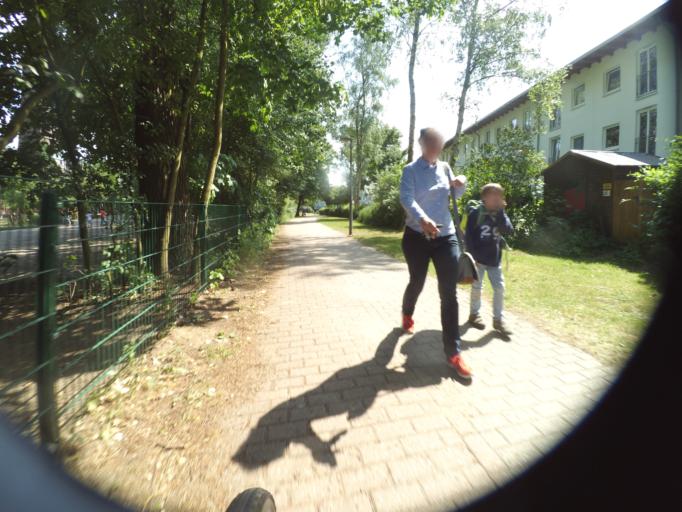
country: DE
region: Hamburg
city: Eidelstedt
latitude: 53.5738
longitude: 9.8678
